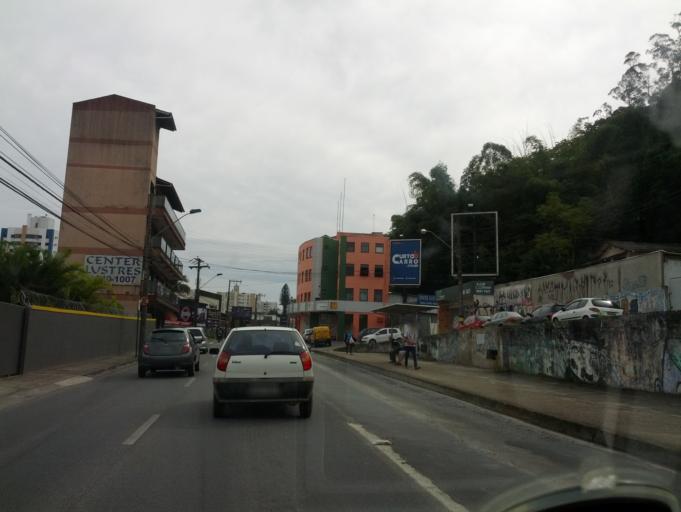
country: BR
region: Santa Catarina
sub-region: Blumenau
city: Blumenau
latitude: -26.9111
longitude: -49.0710
